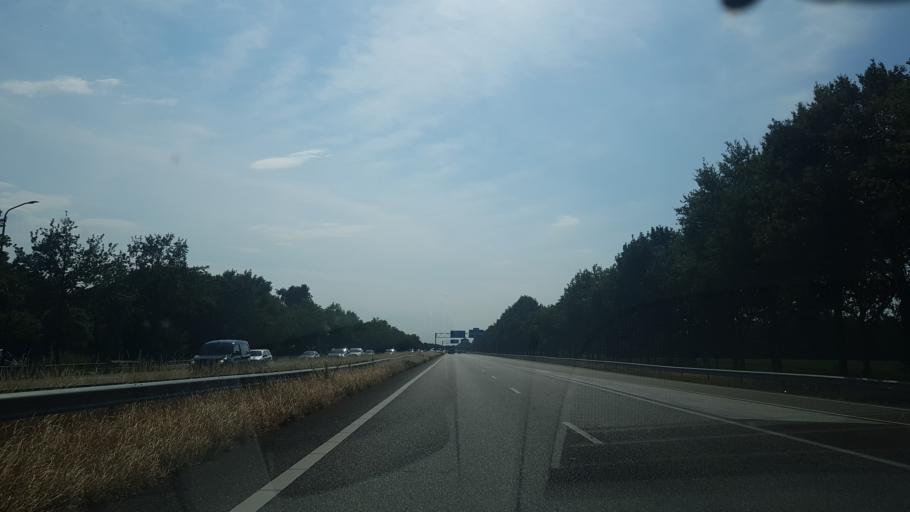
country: NL
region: North Brabant
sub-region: Gemeente Rucphen
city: Rucphen
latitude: 51.5476
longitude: 4.5257
